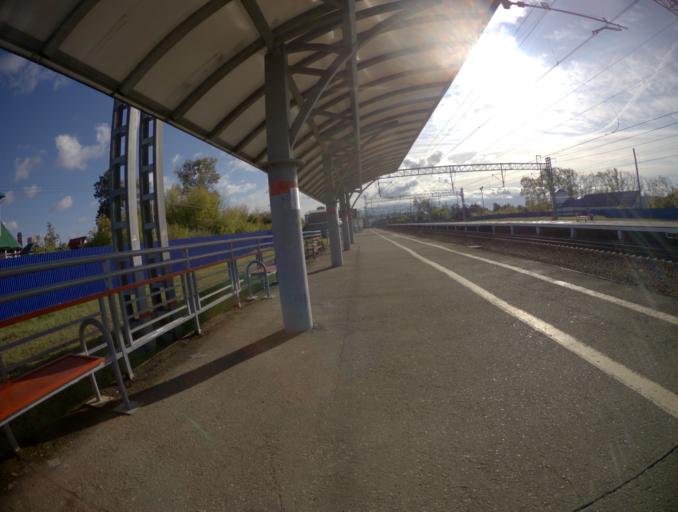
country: RU
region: Vladimir
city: Petushki
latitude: 55.9249
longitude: 39.4603
